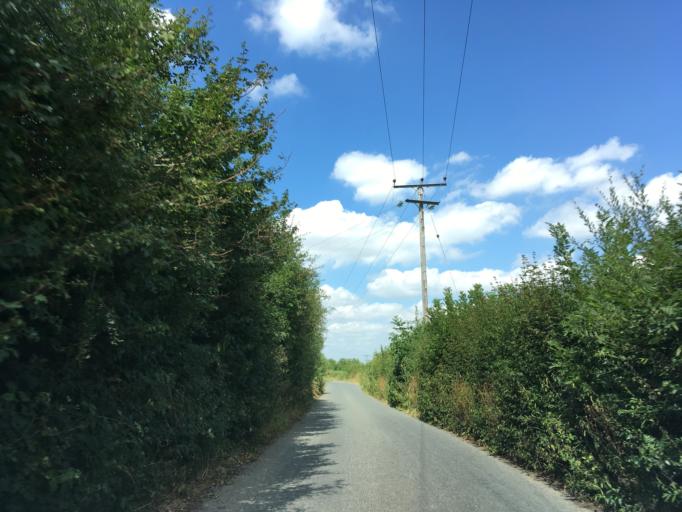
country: GB
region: England
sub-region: Gloucestershire
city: Shurdington
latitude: 51.8523
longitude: -2.1289
